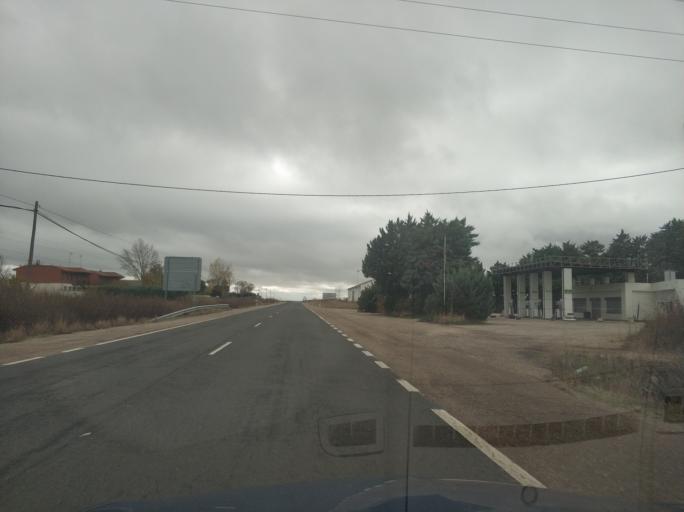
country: ES
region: Castille and Leon
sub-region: Provincia de Salamanca
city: Pedrosillo el Ralo
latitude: 41.0588
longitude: -5.5493
